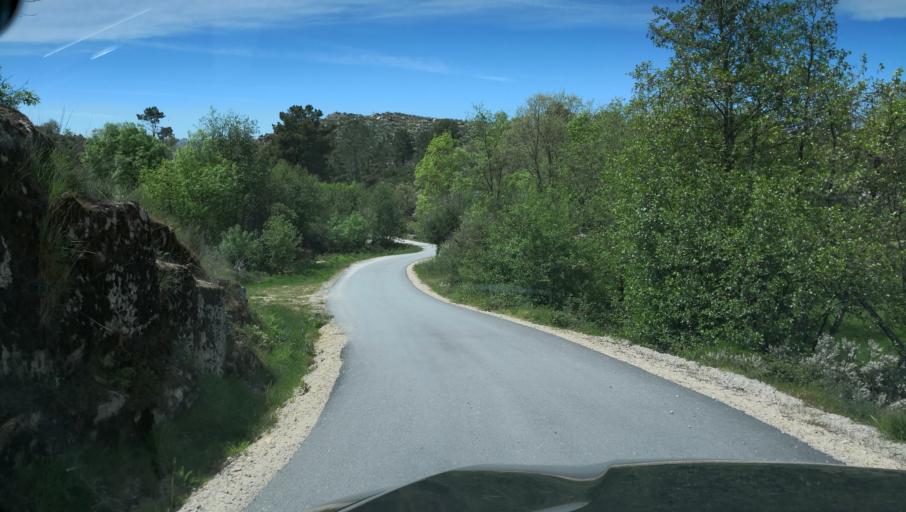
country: PT
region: Vila Real
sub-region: Vila Real
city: Vila Real
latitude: 41.3664
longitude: -7.6700
